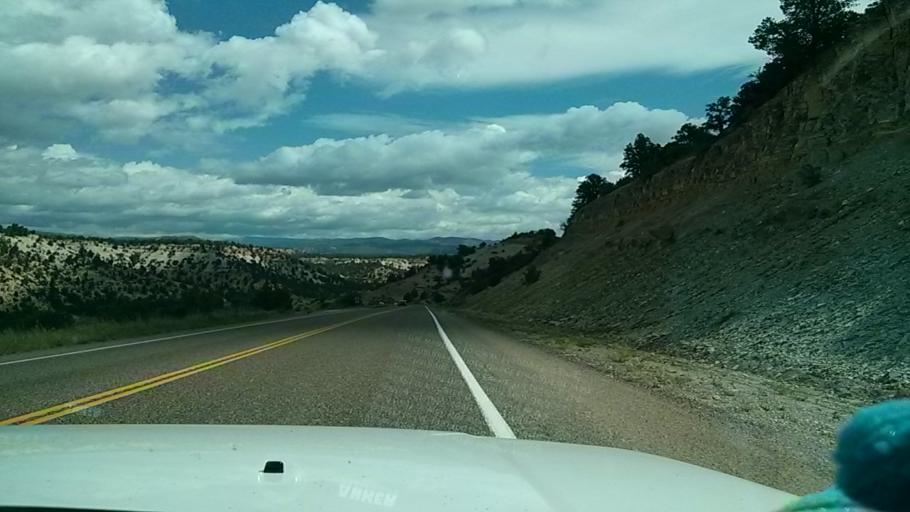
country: US
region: Utah
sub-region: Kane County
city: Kanab
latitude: 37.2069
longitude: -112.6848
